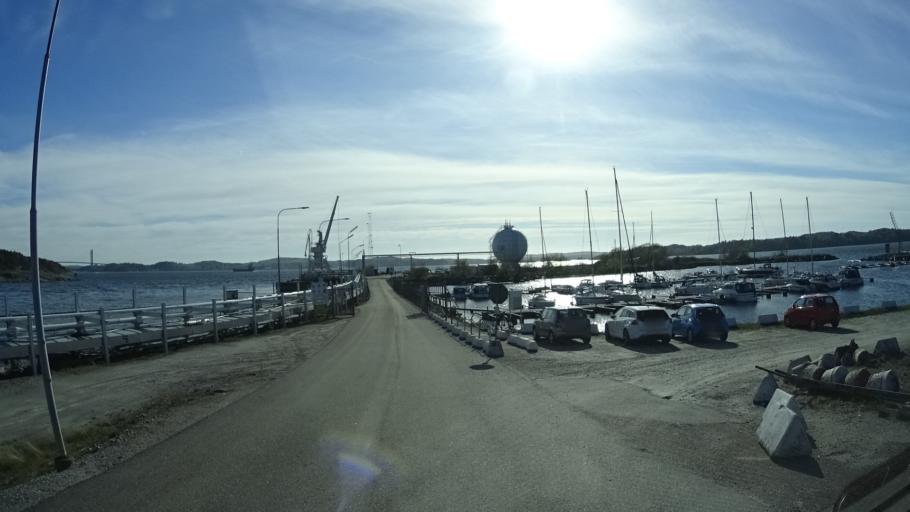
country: SE
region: Vaestra Goetaland
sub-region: Stenungsunds Kommun
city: Stenungsund
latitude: 58.0830
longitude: 11.8037
